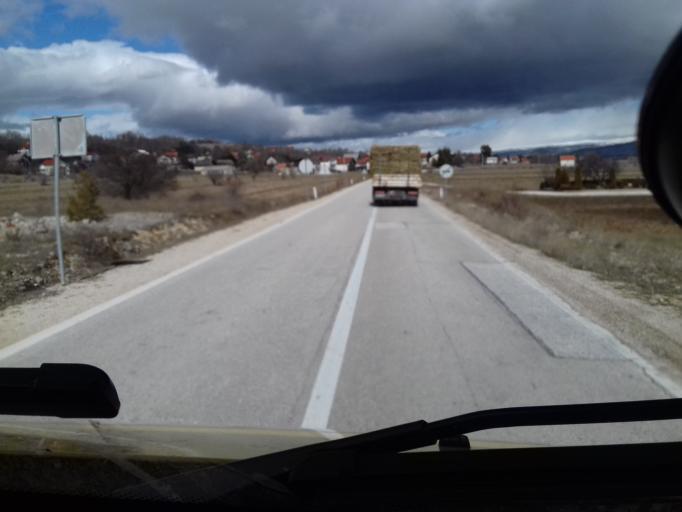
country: BA
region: Federation of Bosnia and Herzegovina
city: Dreznica
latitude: 43.5917
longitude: 17.2736
